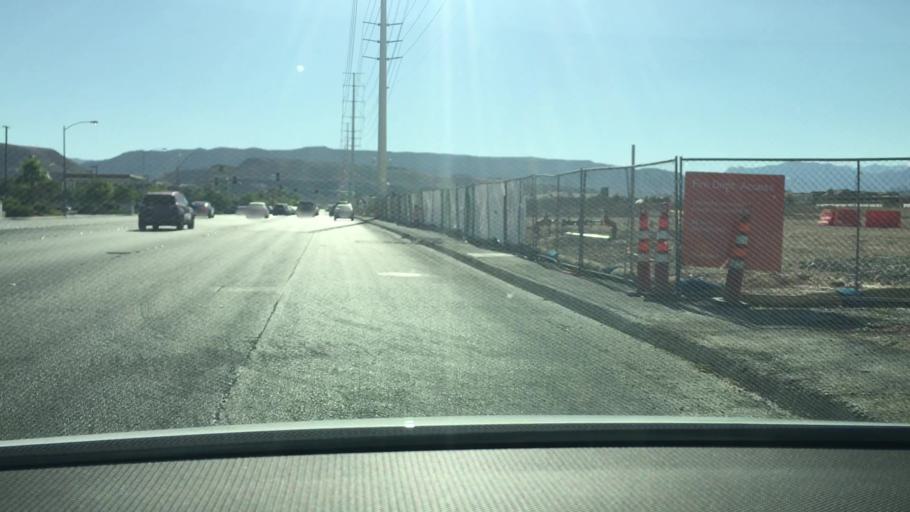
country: US
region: Nevada
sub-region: Clark County
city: Summerlin South
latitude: 36.0852
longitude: -115.2953
